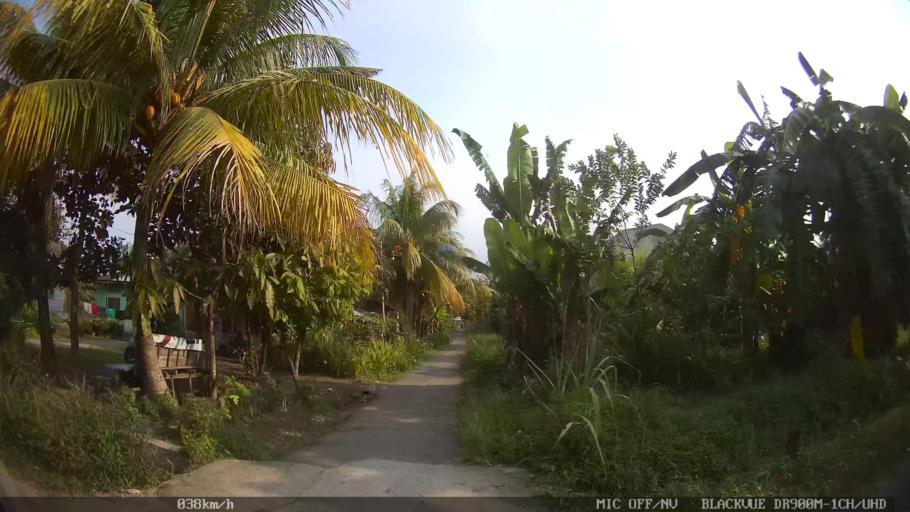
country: ID
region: North Sumatra
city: Binjai
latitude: 3.6174
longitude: 98.5274
